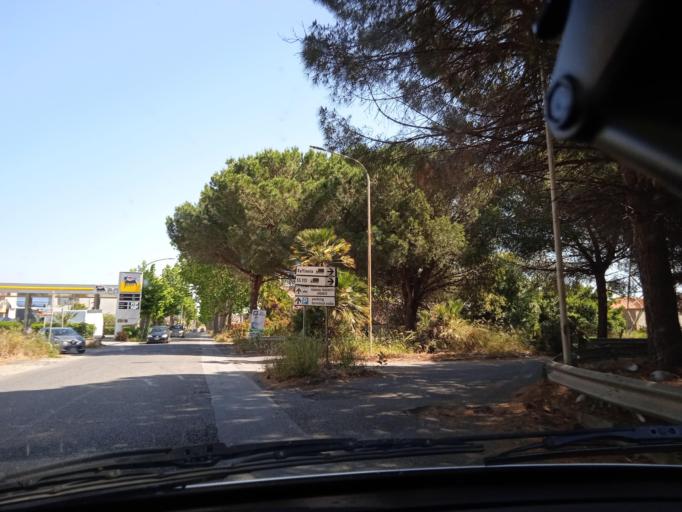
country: IT
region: Sicily
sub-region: Messina
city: Milazzo
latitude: 38.1997
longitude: 15.2530
